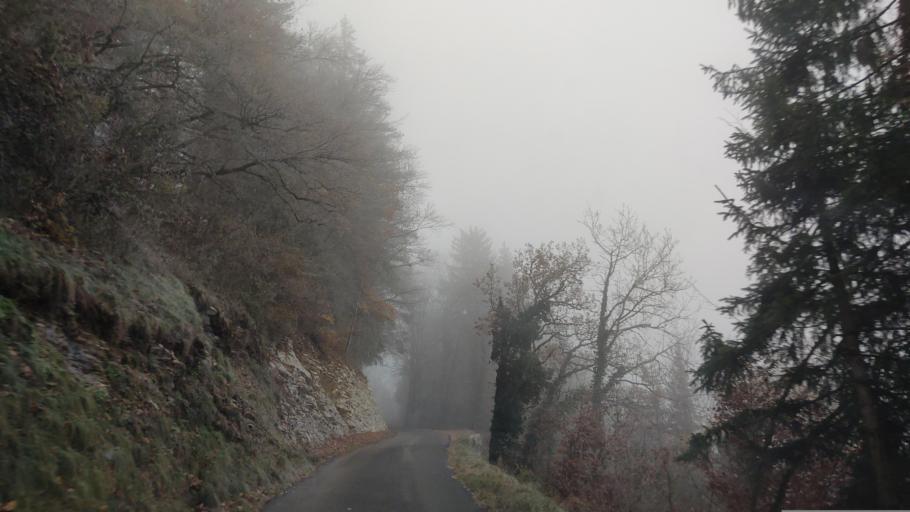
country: FR
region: Rhone-Alpes
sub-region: Departement de la Haute-Savoie
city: Doussard
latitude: 45.6894
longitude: 6.1431
